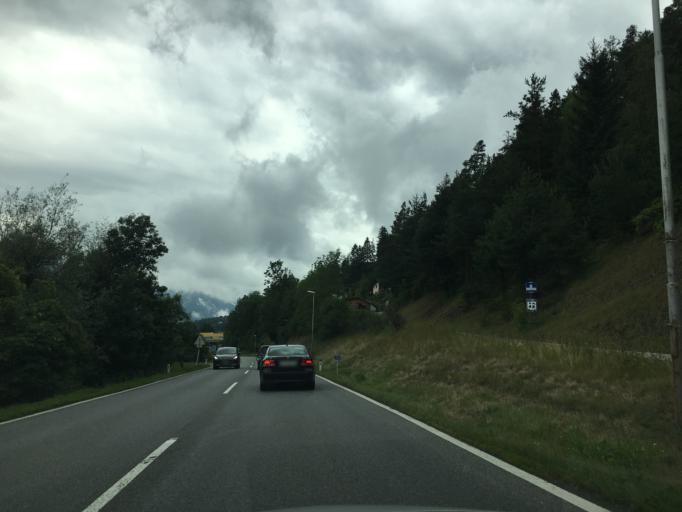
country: AT
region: Tyrol
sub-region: Politischer Bezirk Imst
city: Imst
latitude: 47.2520
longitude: 10.7475
